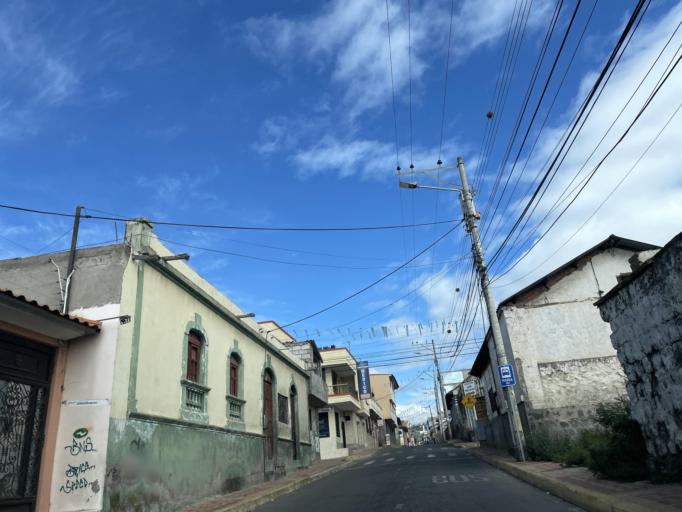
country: EC
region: Chimborazo
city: Guano
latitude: -1.6077
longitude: -78.6370
